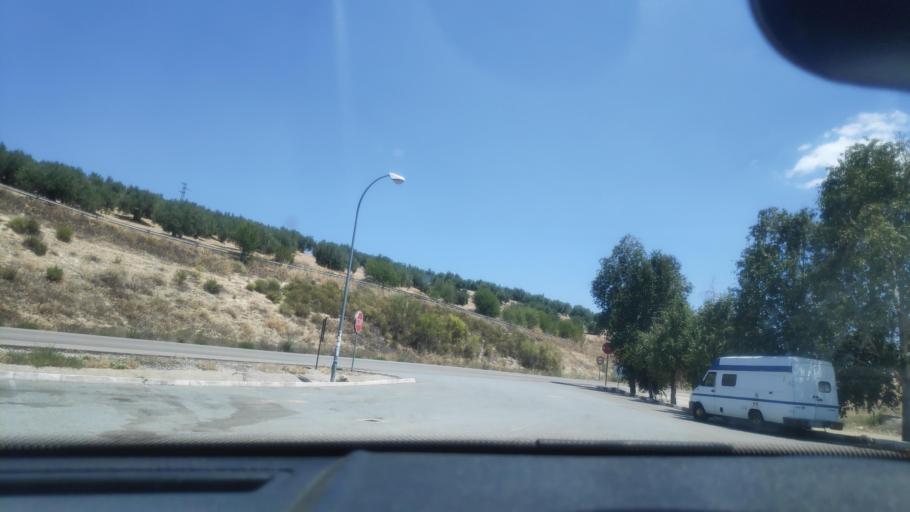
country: ES
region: Andalusia
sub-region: Provincia de Granada
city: Campotejar
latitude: 37.4874
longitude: -3.6017
